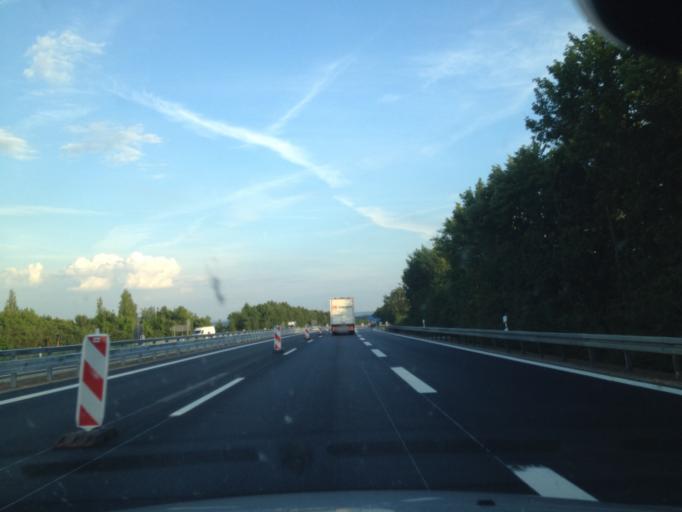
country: DE
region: Bavaria
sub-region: Regierungsbezirk Unterfranken
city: Biebelried
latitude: 49.7616
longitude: 10.1045
